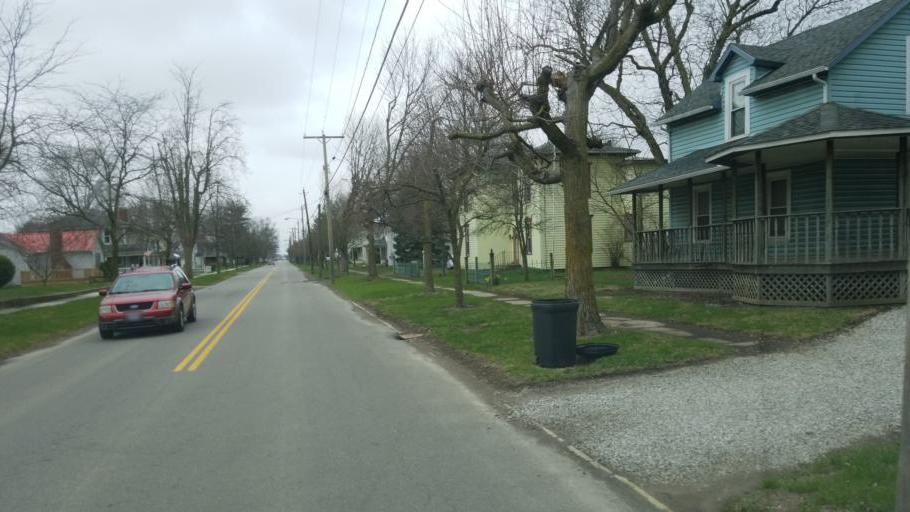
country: US
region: Ohio
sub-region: Union County
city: Richwood
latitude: 40.4258
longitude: -83.3025
